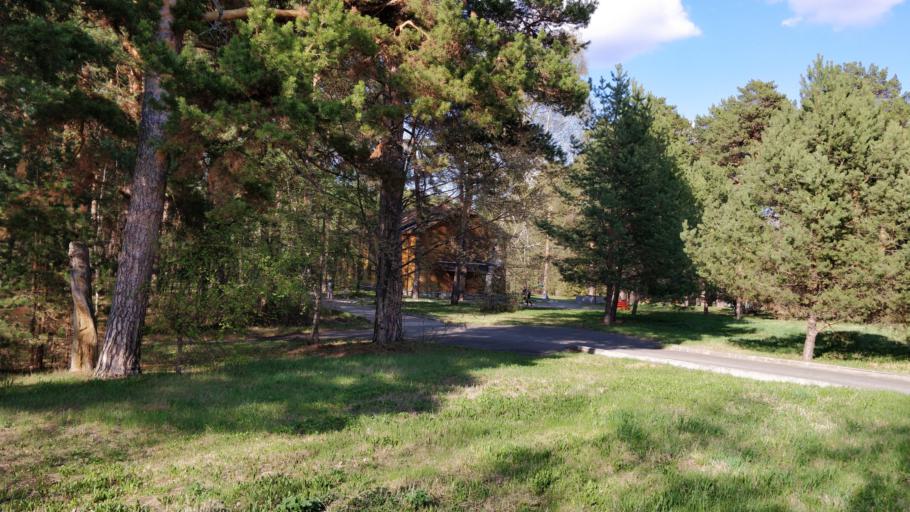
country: RU
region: Perm
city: Ust'-Kachka
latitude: 58.0061
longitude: 55.6657
